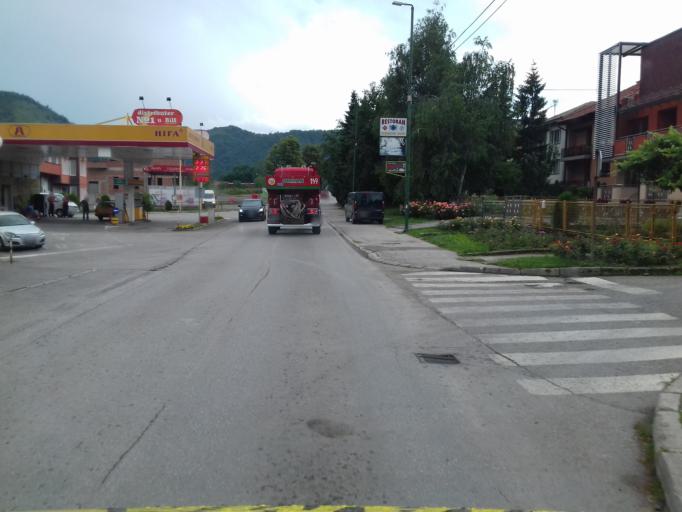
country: BA
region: Federation of Bosnia and Herzegovina
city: Visoko
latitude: 43.9807
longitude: 18.1836
